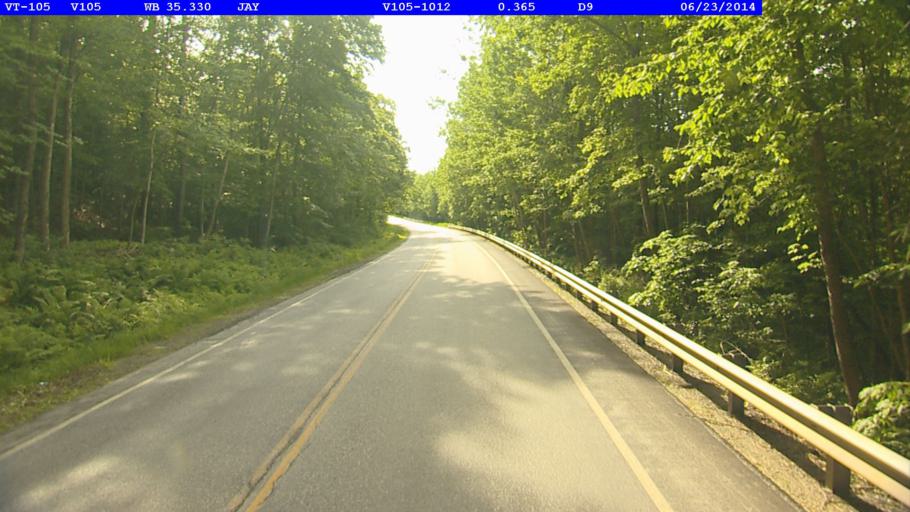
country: US
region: Vermont
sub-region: Franklin County
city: Richford
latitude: 44.9857
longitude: -72.5418
